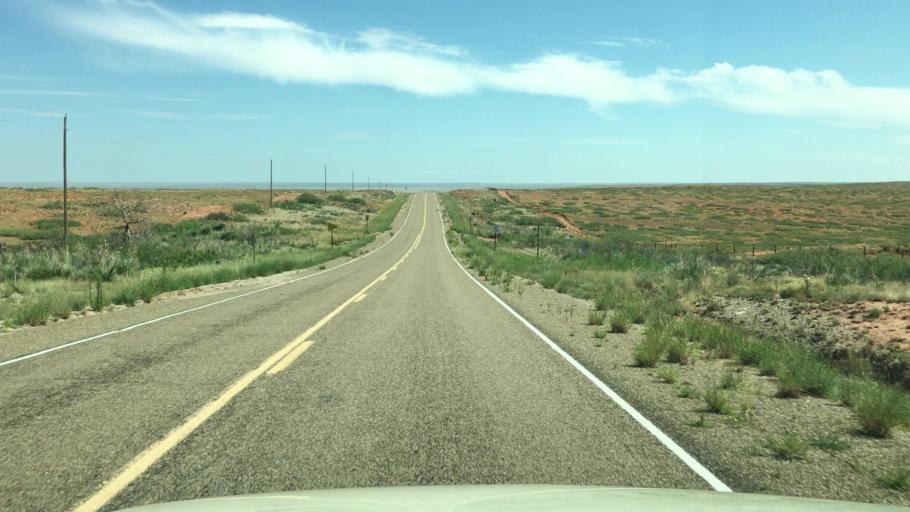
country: US
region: New Mexico
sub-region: Chaves County
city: Roswell
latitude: 33.9723
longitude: -104.5786
